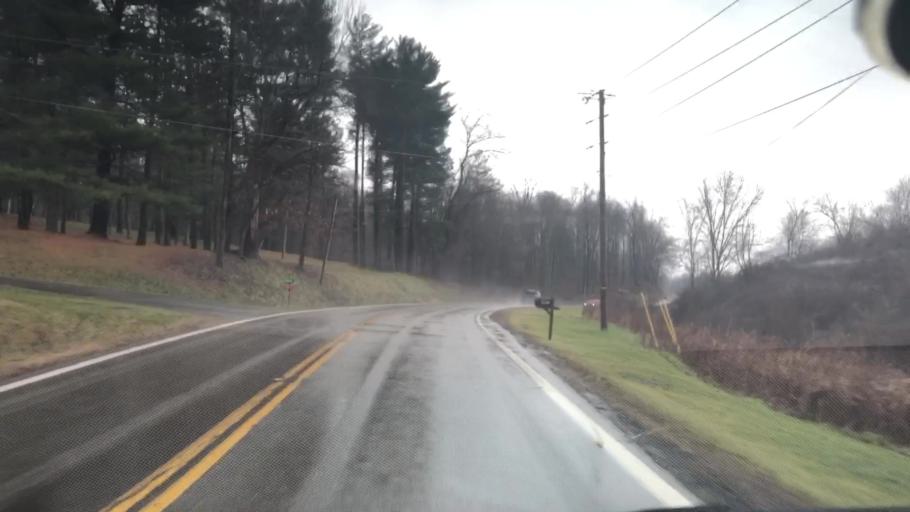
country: US
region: Ohio
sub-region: Harrison County
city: Cadiz
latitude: 40.1662
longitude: -80.9827
